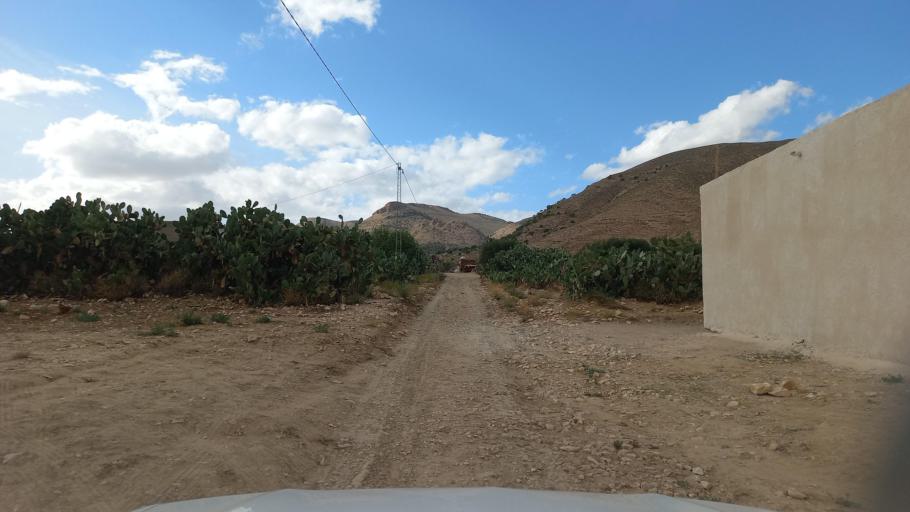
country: TN
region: Al Qasrayn
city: Sbiba
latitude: 35.4512
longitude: 9.0648
